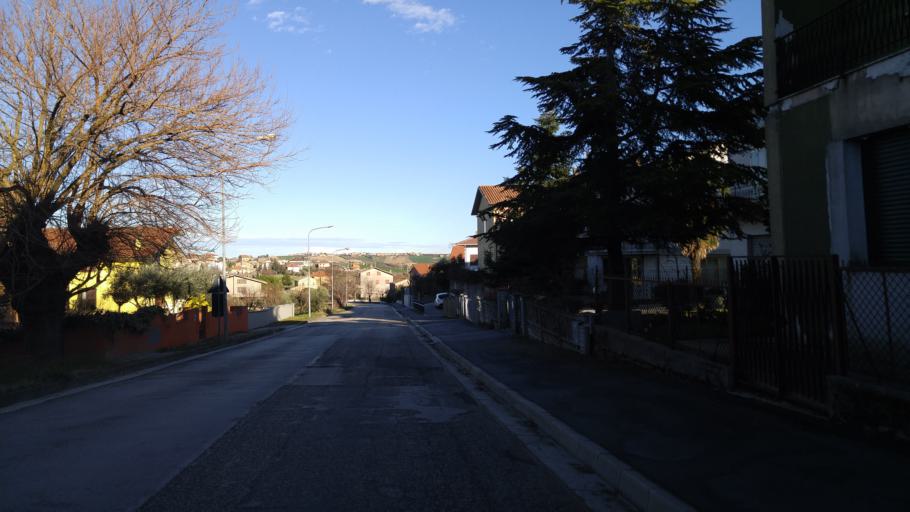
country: IT
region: The Marches
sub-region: Provincia di Pesaro e Urbino
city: Bellocchi
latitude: 43.7537
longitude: 13.0158
